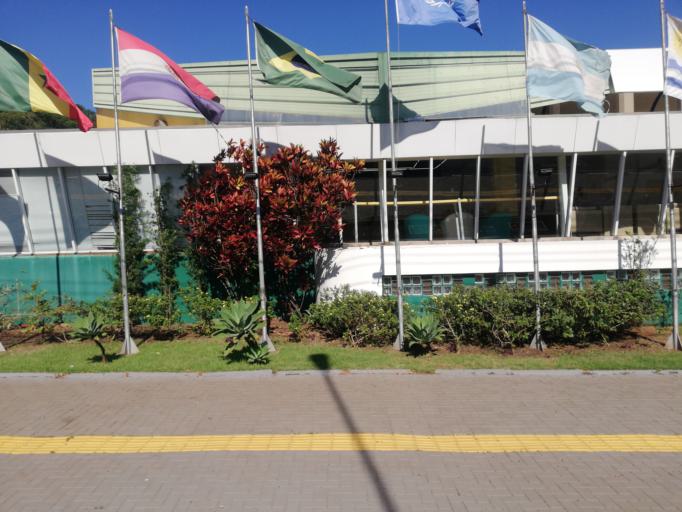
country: BR
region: Parana
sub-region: Foz Do Iguacu
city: Foz do Iguacu
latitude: -25.5532
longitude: -54.5694
